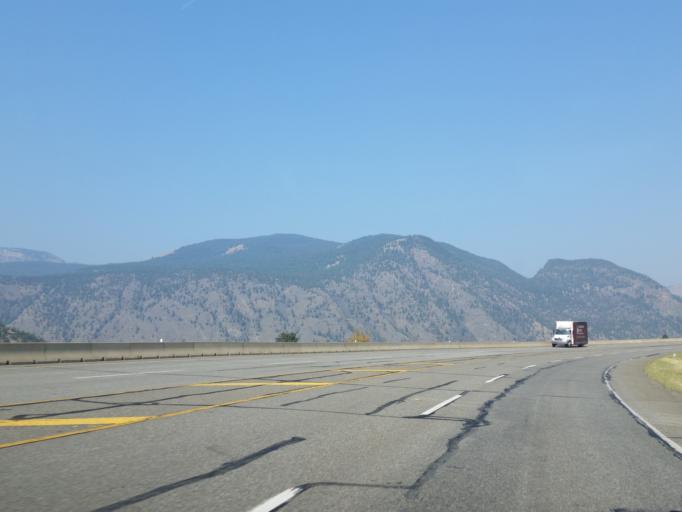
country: CA
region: British Columbia
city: Oliver
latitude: 49.2208
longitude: -119.9543
